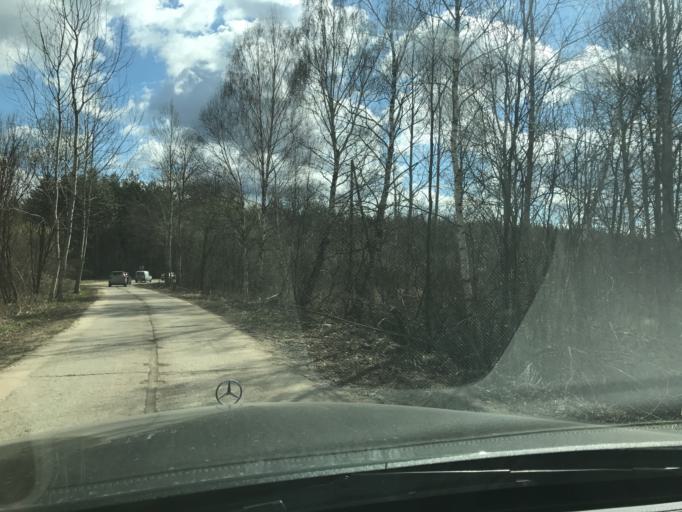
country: RU
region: Moskovskaya
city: Vereya
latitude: 55.8392
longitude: 39.0819
